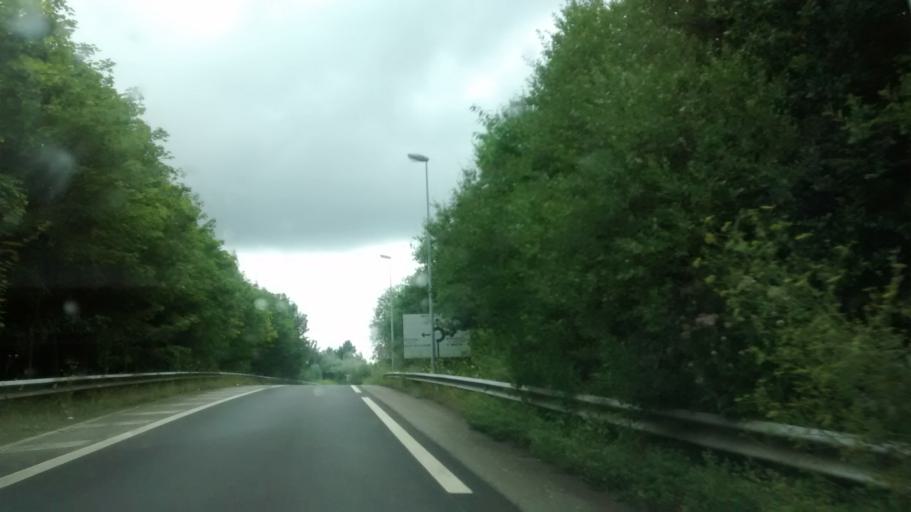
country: FR
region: Haute-Normandie
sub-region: Departement de la Seine-Maritime
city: Bois-Guillaume
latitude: 49.4658
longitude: 1.1354
